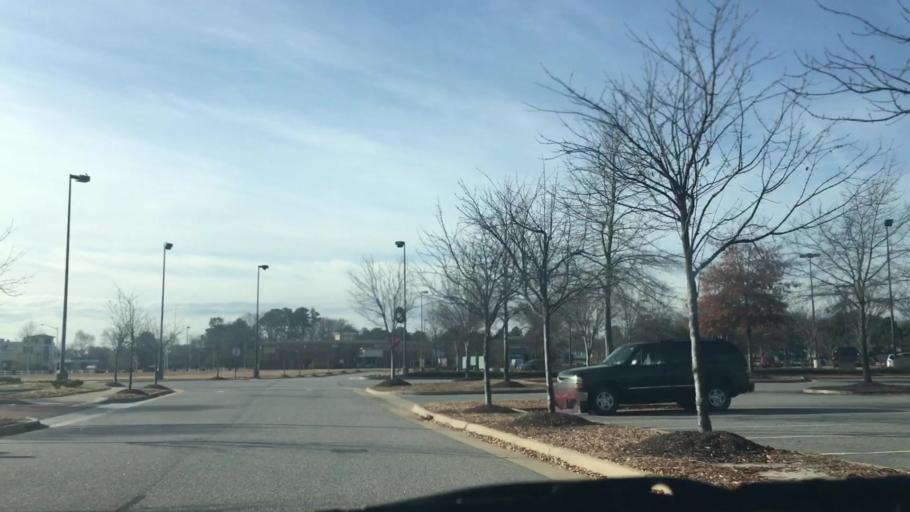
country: US
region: Virginia
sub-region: City of Chesapeake
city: Chesapeake
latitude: 36.8070
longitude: -76.1310
